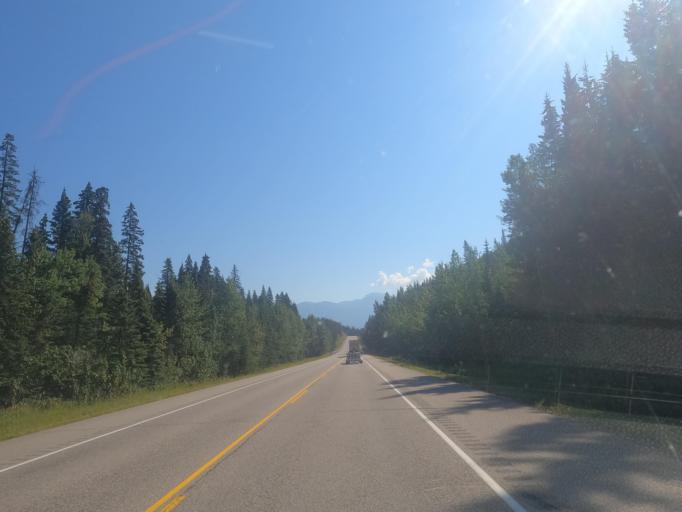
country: CA
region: Alberta
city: Jasper Park Lodge
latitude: 52.8609
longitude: -118.1907
